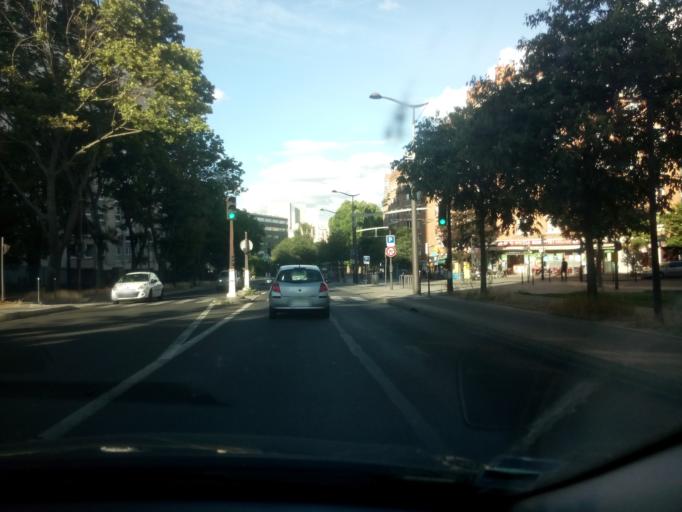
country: FR
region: Ile-de-France
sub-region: Departement du Val-de-Marne
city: Gentilly
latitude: 48.8205
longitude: 2.3487
